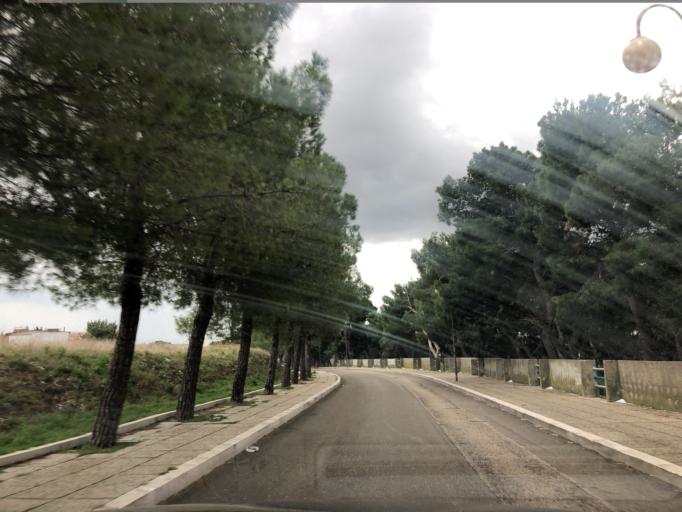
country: IT
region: Apulia
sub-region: Provincia di Foggia
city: Lucera
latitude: 41.5074
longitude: 15.3237
